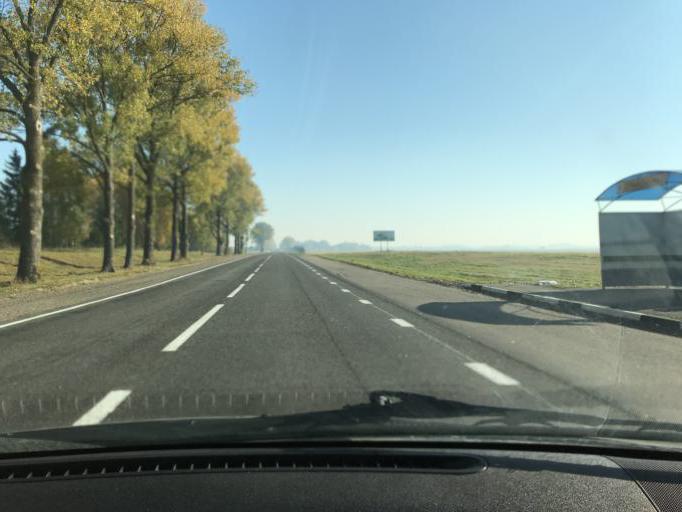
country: BY
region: Minsk
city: Klyetsk
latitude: 52.9729
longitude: 26.7153
